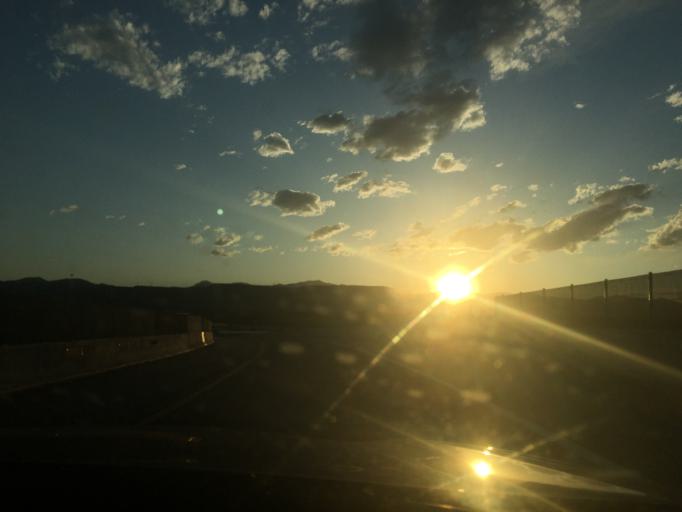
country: US
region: Colorado
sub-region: Jefferson County
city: Applewood
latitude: 39.7754
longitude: -105.1446
